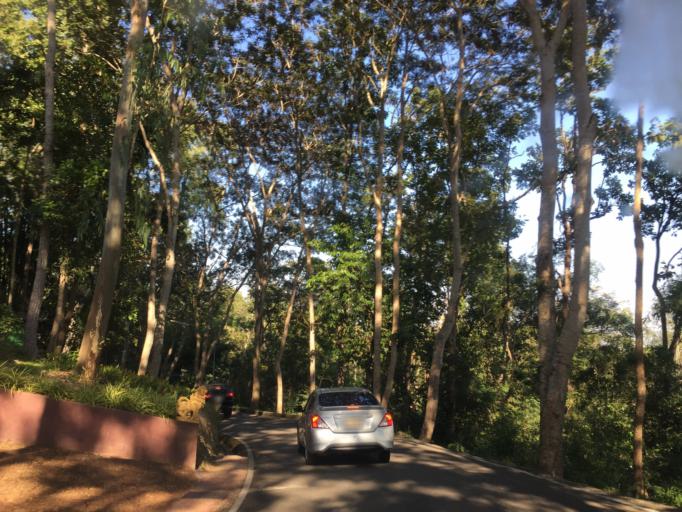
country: TH
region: Chiang Mai
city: Chiang Mai
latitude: 18.8068
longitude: 98.9458
